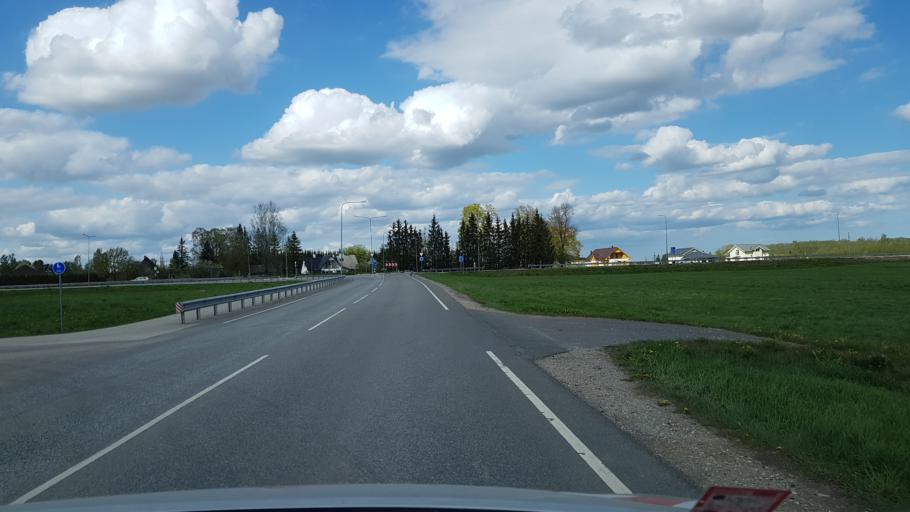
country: EE
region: Tartu
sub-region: Tartu linn
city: Tartu
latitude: 58.3711
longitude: 26.7993
